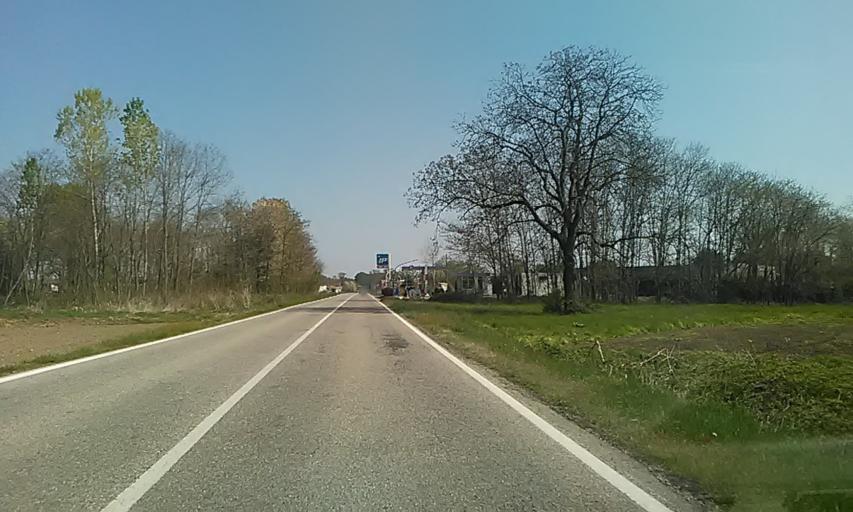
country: IT
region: Piedmont
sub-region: Provincia di Vercelli
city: Lenta
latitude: 45.5590
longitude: 8.3795
